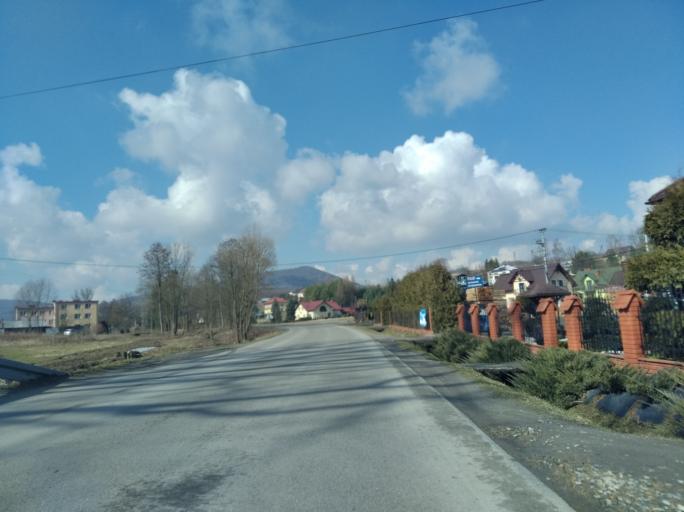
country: PL
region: Subcarpathian Voivodeship
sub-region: Powiat strzyzowski
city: Frysztak
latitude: 49.8715
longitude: 21.5955
